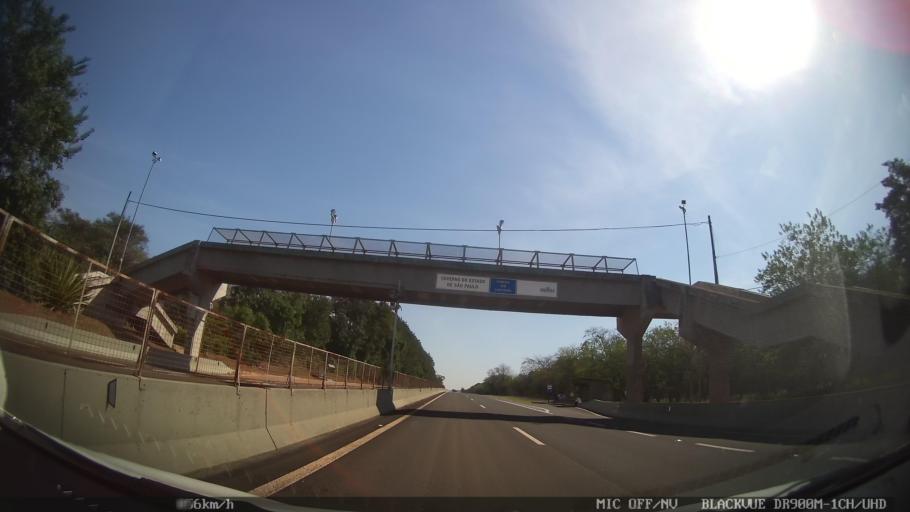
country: BR
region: Sao Paulo
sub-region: Ribeirao Preto
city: Ribeirao Preto
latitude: -21.1730
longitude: -47.8599
